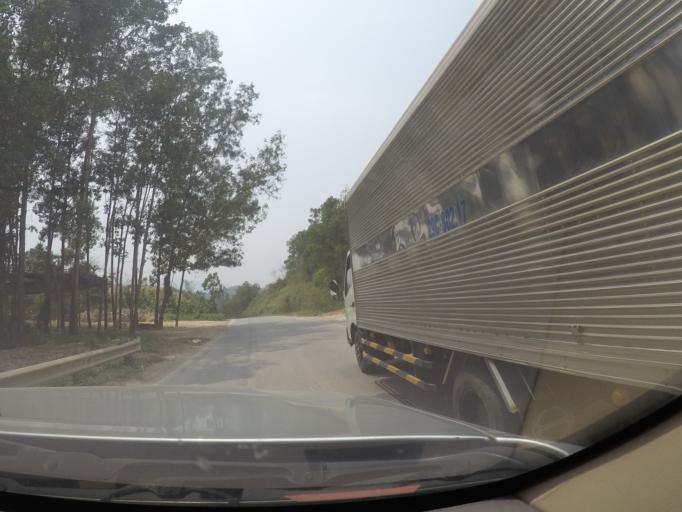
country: VN
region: Thanh Hoa
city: Thi Tran Yen Cat
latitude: 19.6708
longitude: 105.4396
